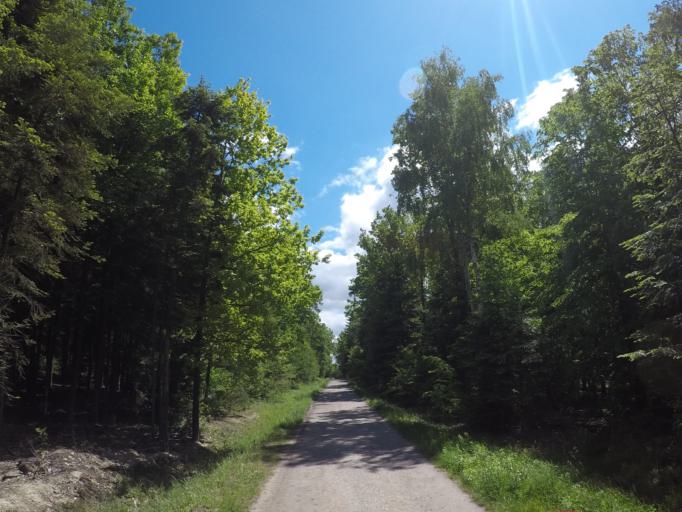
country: PL
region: Swietokrzyskie
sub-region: Powiat kielecki
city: Domaszowice
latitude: 50.9112
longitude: 20.6584
